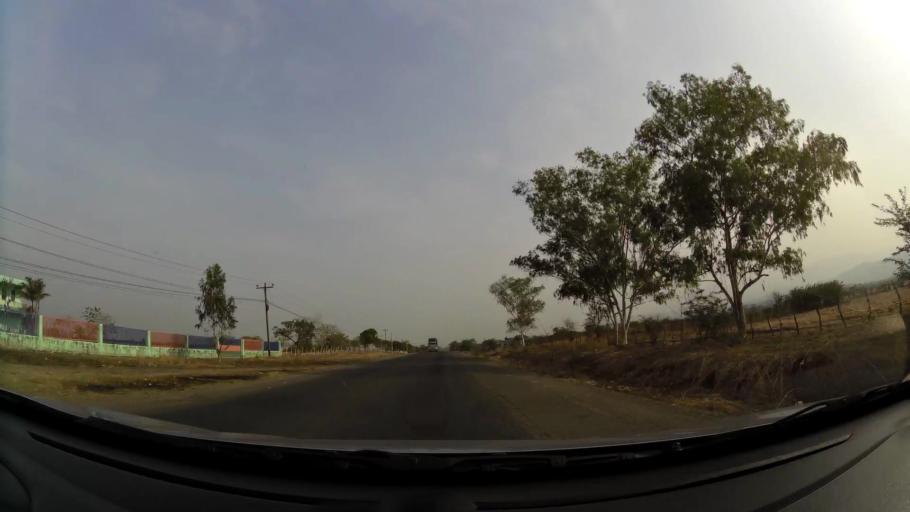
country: HN
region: Comayagua
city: Flores
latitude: 14.3091
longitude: -87.5790
